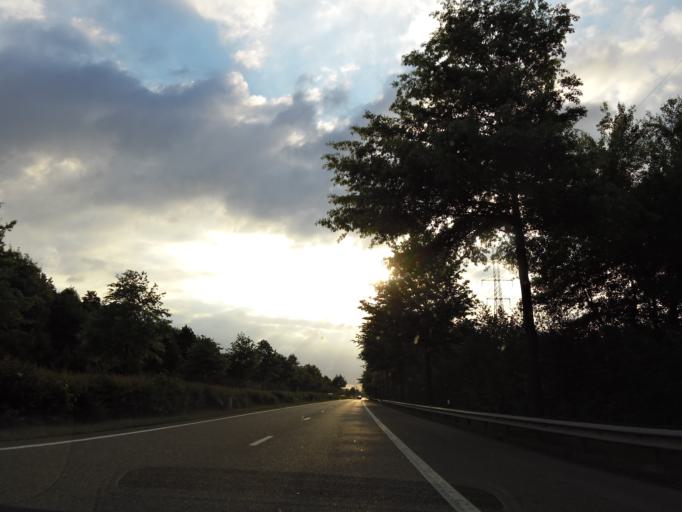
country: BE
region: Flanders
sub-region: Provincie Limburg
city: Diepenbeek
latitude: 50.9344
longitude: 5.4418
